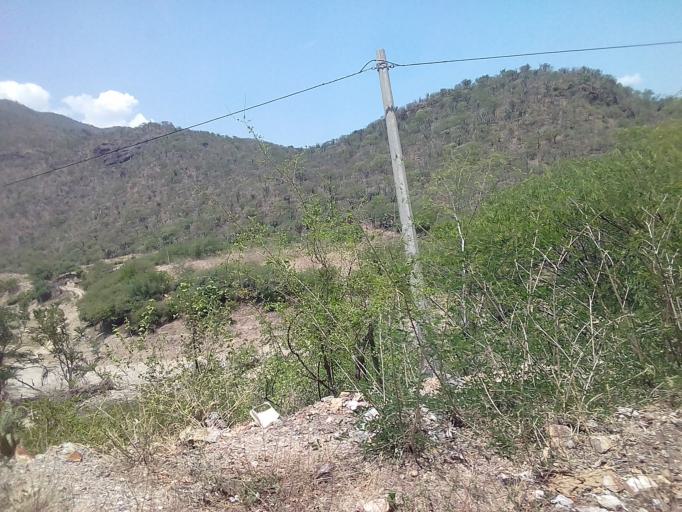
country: MX
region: Oaxaca
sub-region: San Pedro Quiatoni
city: San Pedro Quiatoni
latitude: 16.6772
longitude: -96.1479
